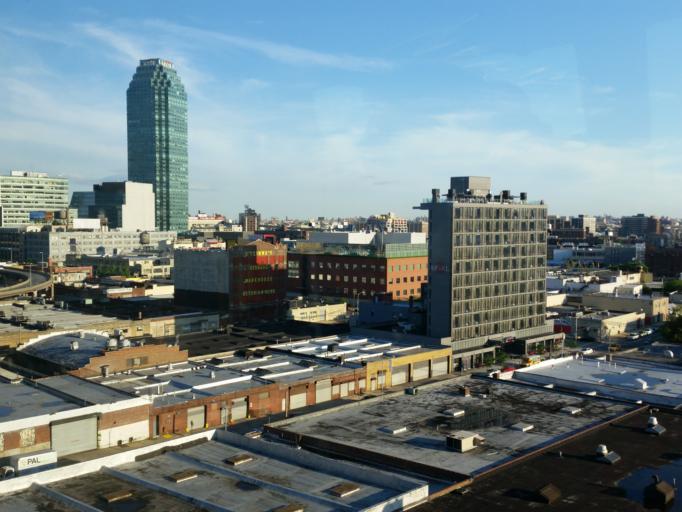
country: US
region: New York
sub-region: Queens County
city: Long Island City
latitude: 40.7538
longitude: -73.9475
